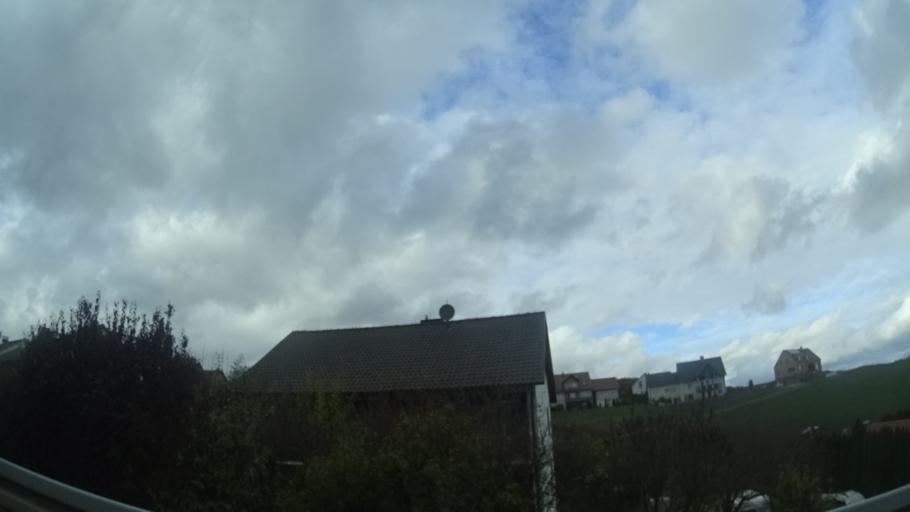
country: DE
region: Bavaria
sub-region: Regierungsbezirk Unterfranken
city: Rodelmaier
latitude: 50.3244
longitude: 10.3076
